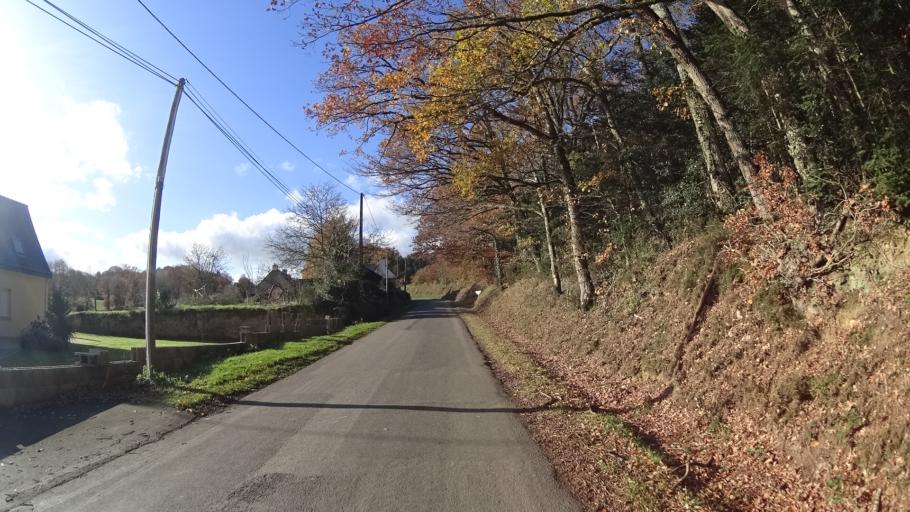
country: FR
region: Brittany
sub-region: Departement du Morbihan
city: Carentoir
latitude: 47.8347
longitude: -2.0786
